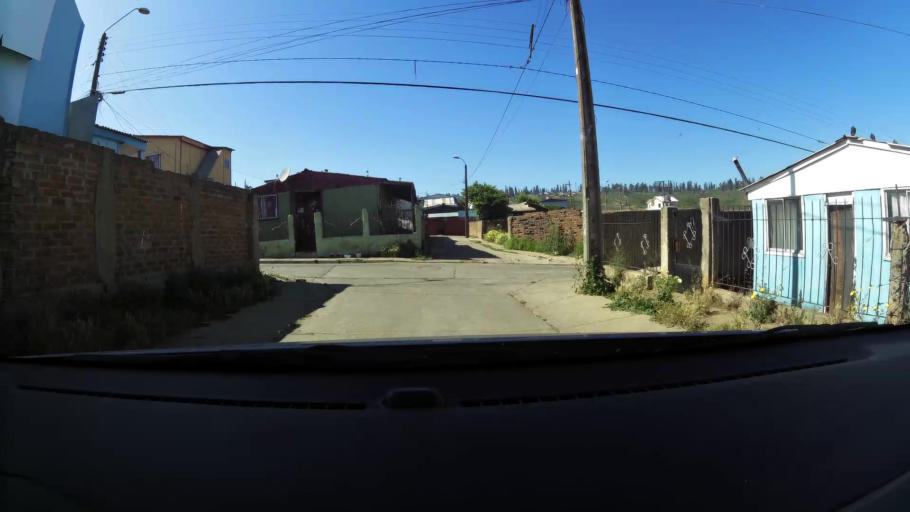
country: CL
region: Valparaiso
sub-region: Provincia de Valparaiso
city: Valparaiso
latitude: -33.0555
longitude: -71.6458
